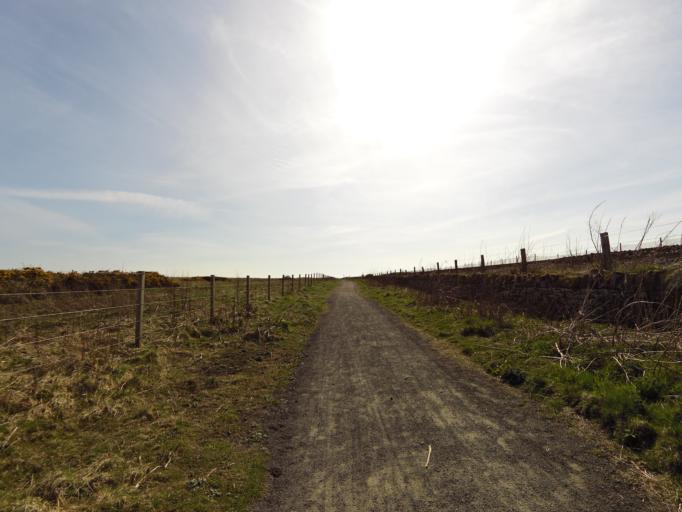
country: GB
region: Scotland
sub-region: Angus
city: Arbroath
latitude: 56.5430
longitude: -2.6210
